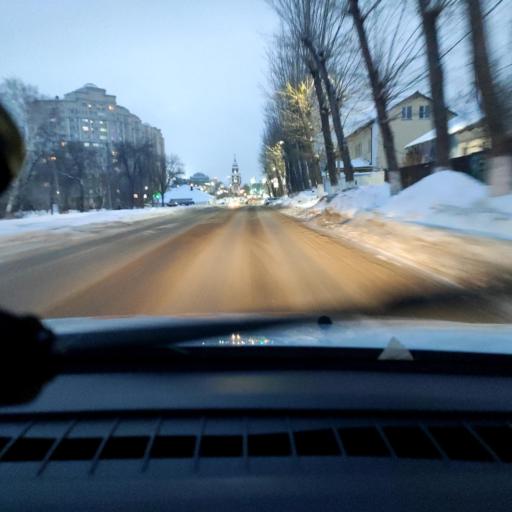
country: RU
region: Samara
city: Novokuybyshevsk
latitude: 53.1046
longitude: 49.9488
